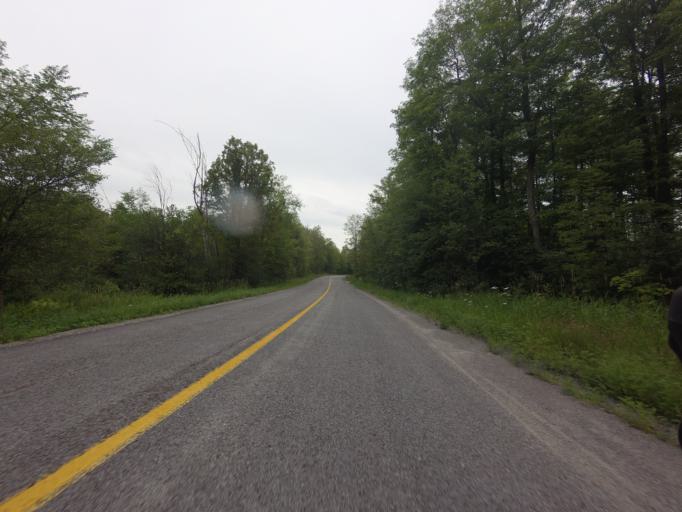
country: CA
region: Ontario
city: Perth
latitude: 44.8800
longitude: -76.5266
